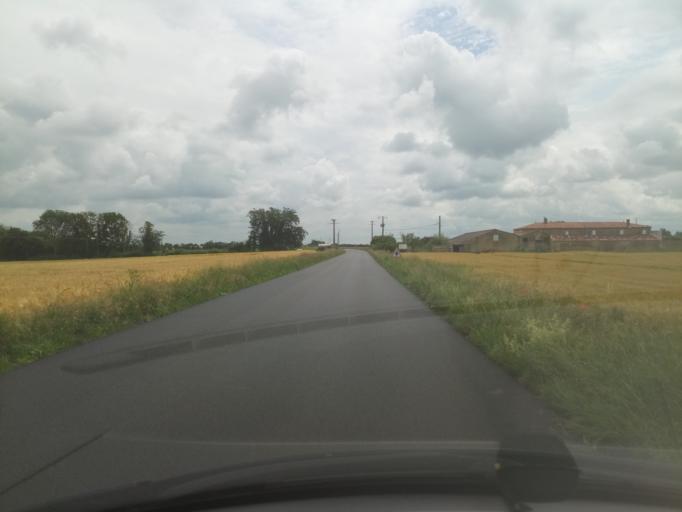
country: FR
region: Poitou-Charentes
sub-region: Departement de la Charente-Maritime
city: Saint-Jean-de-Liversay
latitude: 46.2712
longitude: -0.8960
